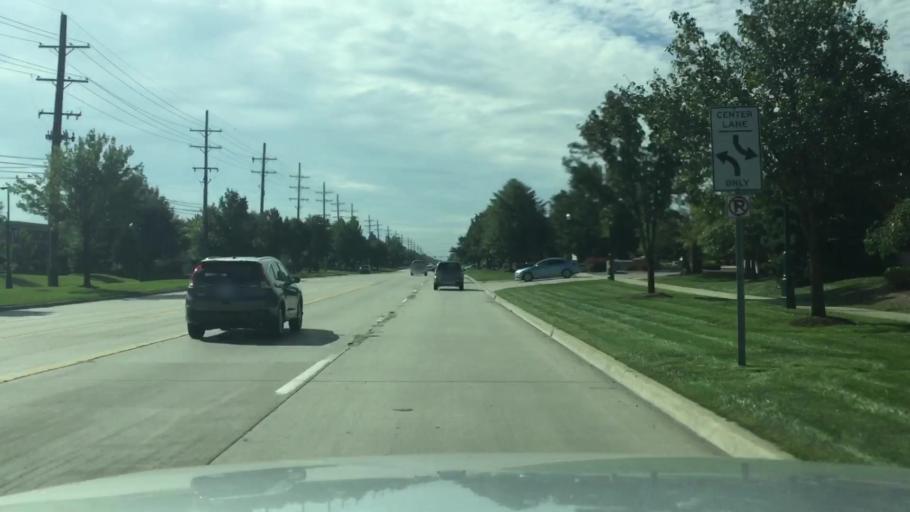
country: US
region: Michigan
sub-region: Wayne County
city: Canton
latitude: 42.3201
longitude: -83.4879
